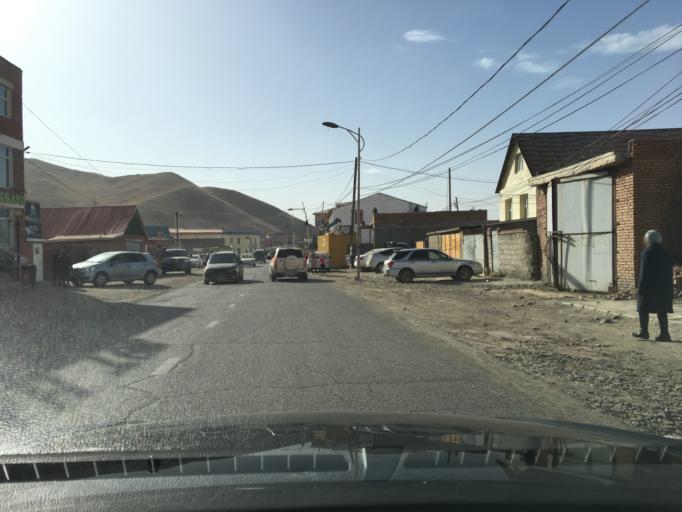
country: MN
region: Ulaanbaatar
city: Ulaanbaatar
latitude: 47.9820
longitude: 106.9391
